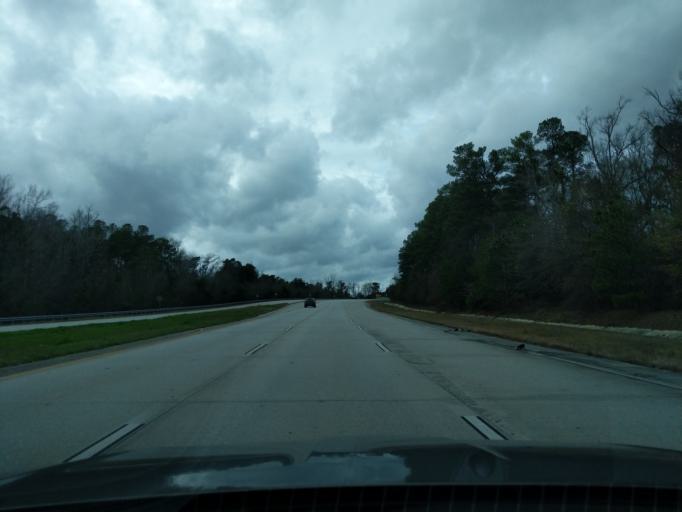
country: US
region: Georgia
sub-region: Columbia County
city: Evans
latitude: 33.4694
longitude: -82.1236
